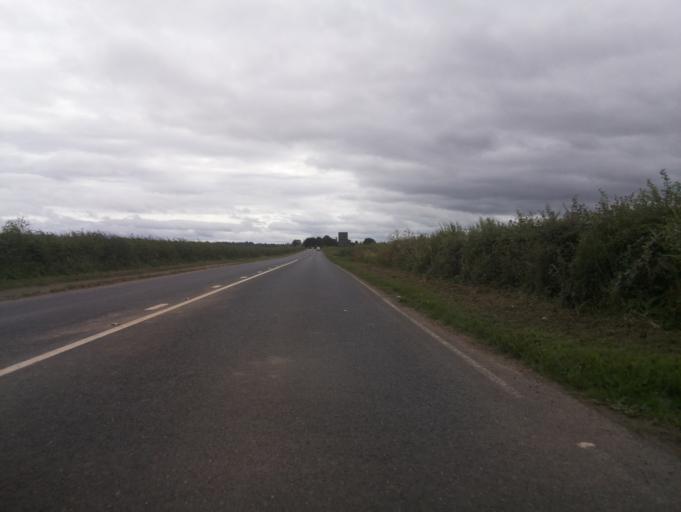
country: GB
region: England
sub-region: Worcestershire
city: Kempsey
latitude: 52.1198
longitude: -2.2232
